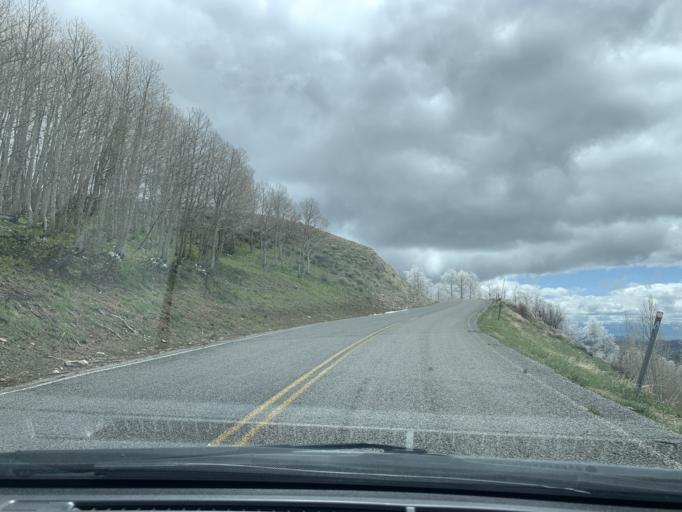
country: US
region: Utah
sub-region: Utah County
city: Santaquin
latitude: 39.8504
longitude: -111.7061
